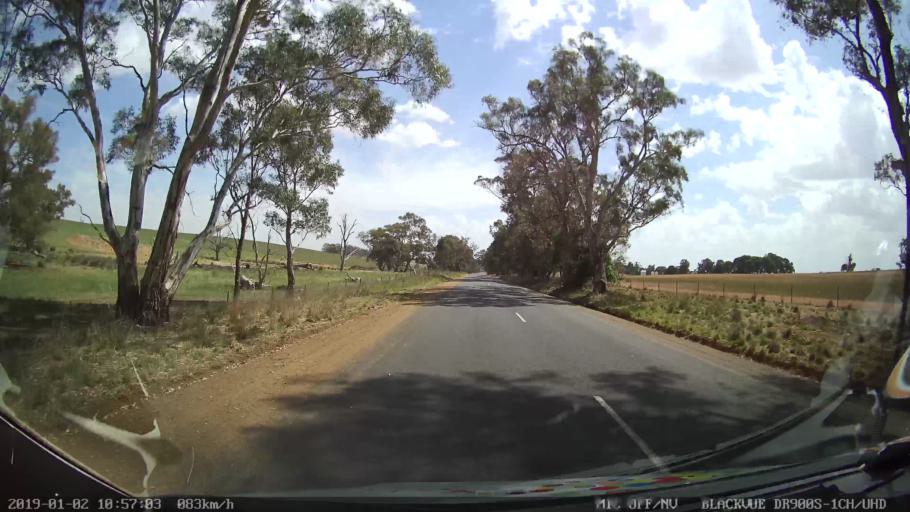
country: AU
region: New South Wales
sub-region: Cootamundra
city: Cootamundra
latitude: -34.6399
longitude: 148.2804
